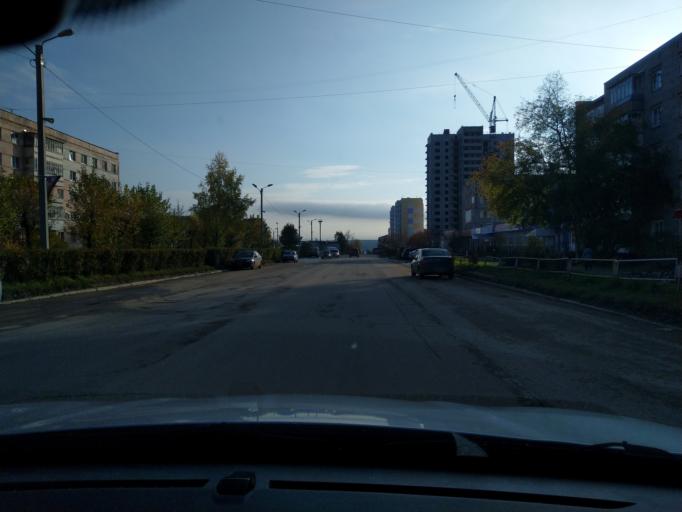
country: RU
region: Perm
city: Dobryanka
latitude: 58.4643
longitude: 56.4010
